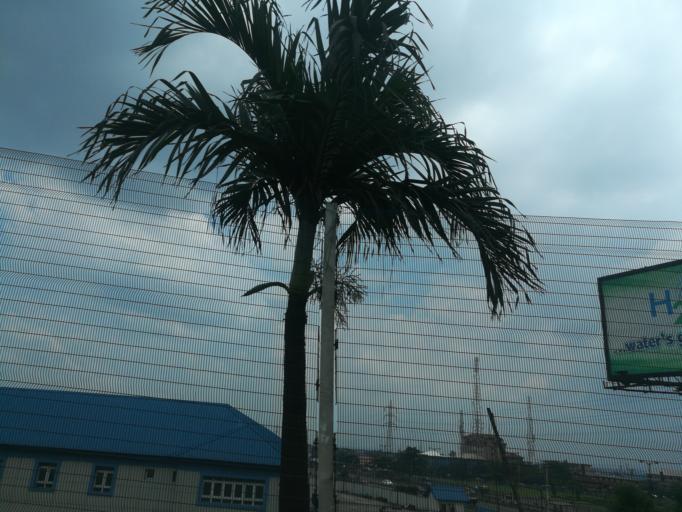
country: NG
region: Lagos
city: Ojota
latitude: 6.5942
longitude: 3.3828
